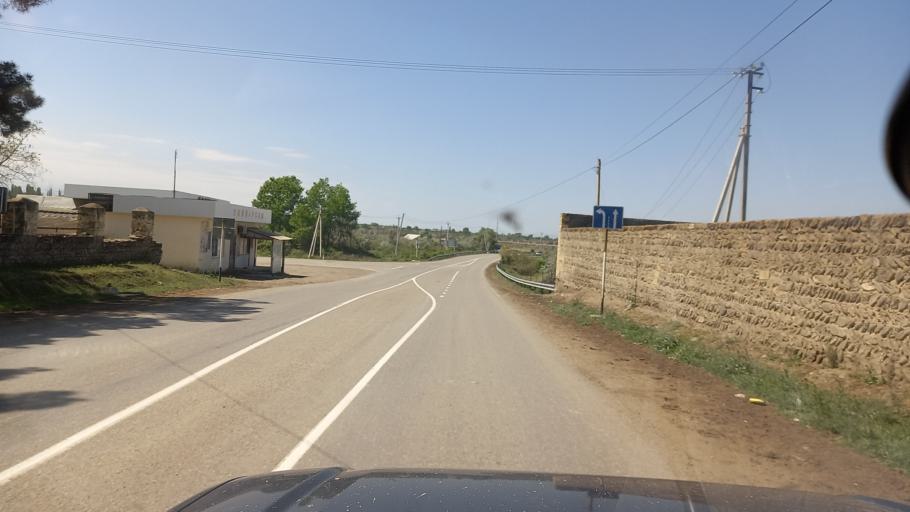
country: AZ
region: Qusar
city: Samur
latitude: 41.7268
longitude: 48.4564
